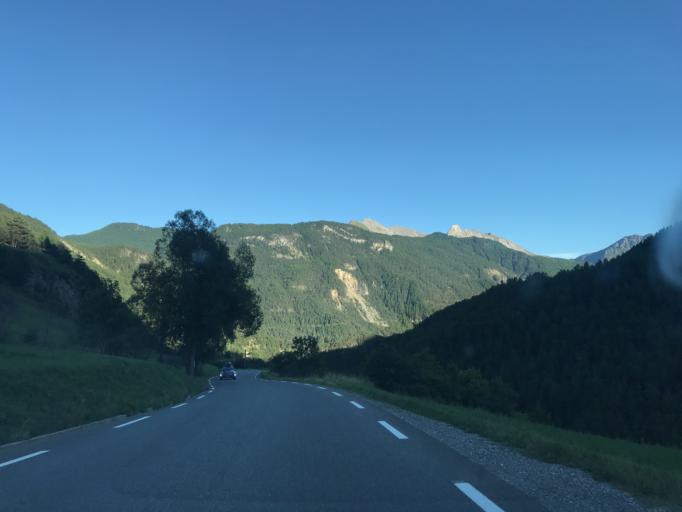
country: FR
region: Provence-Alpes-Cote d'Azur
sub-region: Departement des Hautes-Alpes
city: Guillestre
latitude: 44.7555
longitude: 6.7529
